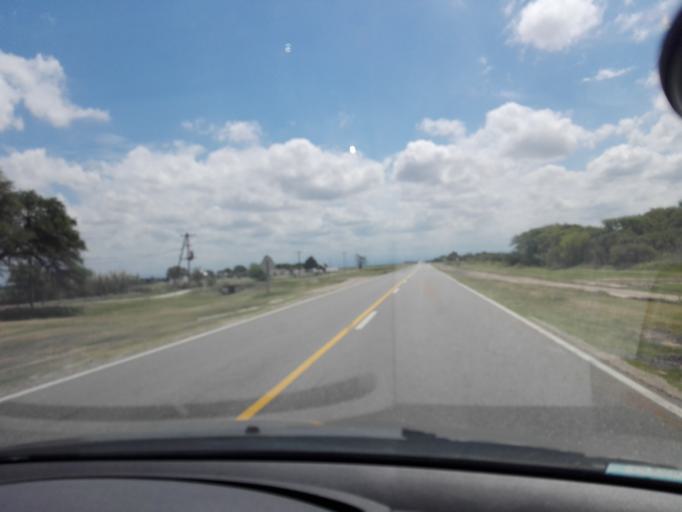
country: AR
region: Cordoba
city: Toledo
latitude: -31.6483
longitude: -64.1036
